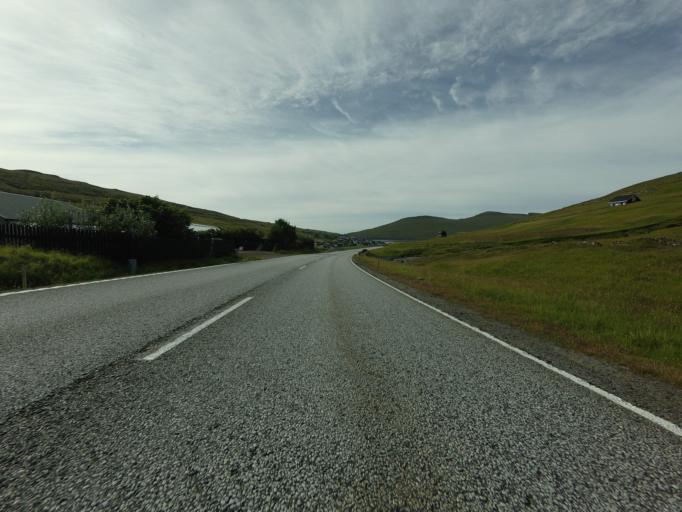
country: FO
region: Vagar
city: Midvagur
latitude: 62.0622
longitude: -7.1477
